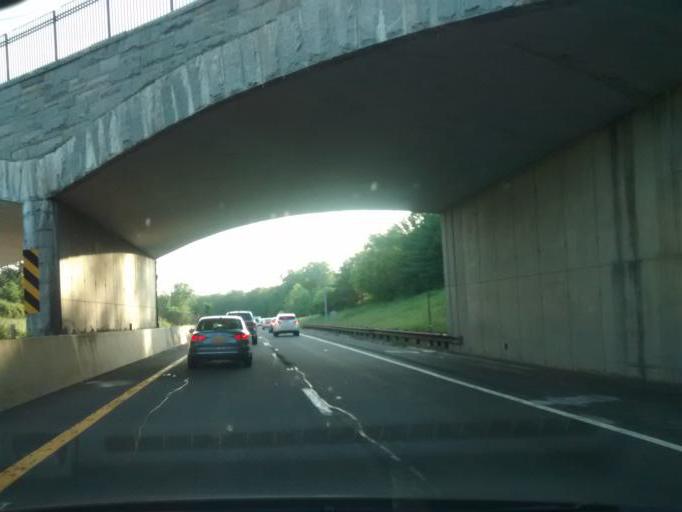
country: US
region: New York
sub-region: Westchester County
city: Rye Brook
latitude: 41.0283
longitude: -73.6833
